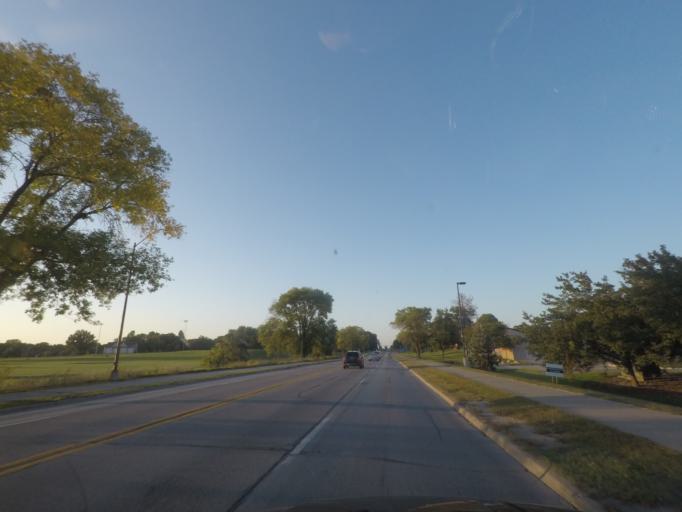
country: US
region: Iowa
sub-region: Story County
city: Ames
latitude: 42.0393
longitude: -93.6448
